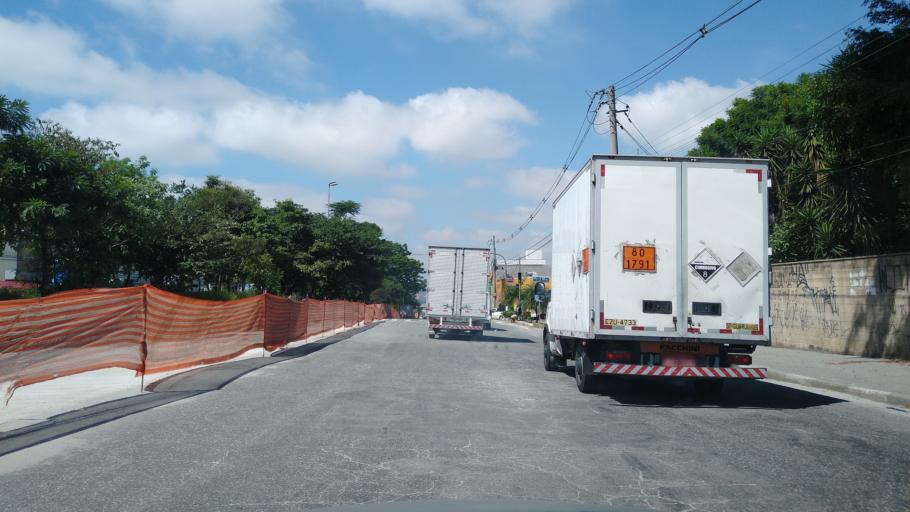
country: BR
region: Sao Paulo
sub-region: Guarulhos
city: Guarulhos
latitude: -23.4582
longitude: -46.4723
